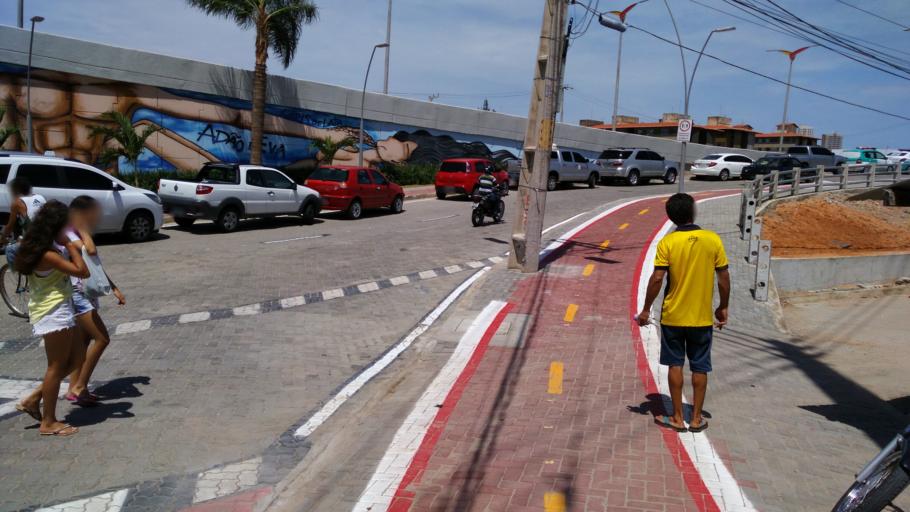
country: BR
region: Ceara
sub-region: Fortaleza
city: Fortaleza
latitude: -3.7637
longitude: -38.5083
